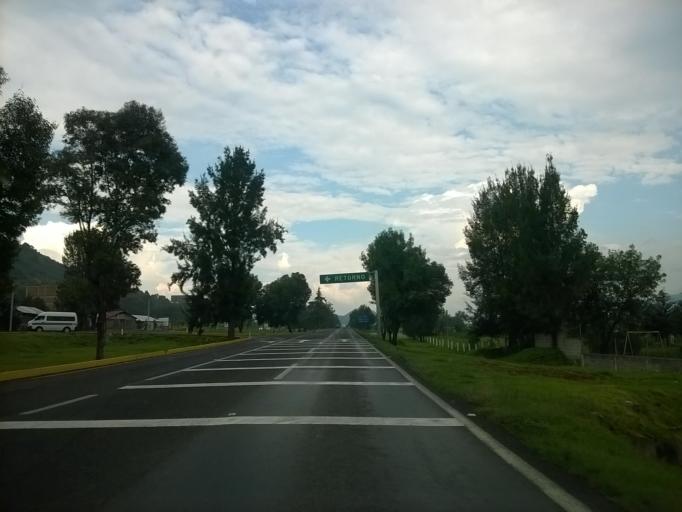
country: MX
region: Michoacan
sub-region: Huiramba
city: El Pedregal
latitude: 19.5316
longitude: -101.4887
